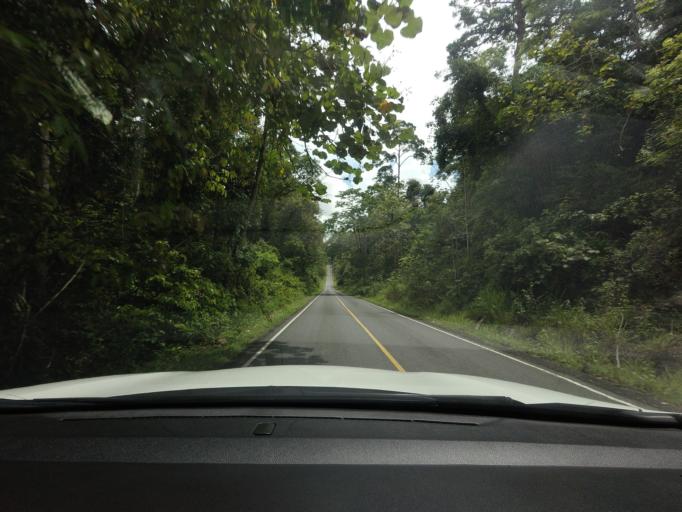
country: TH
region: Nakhon Nayok
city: Nakhon Nayok
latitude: 14.4021
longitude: 101.3675
